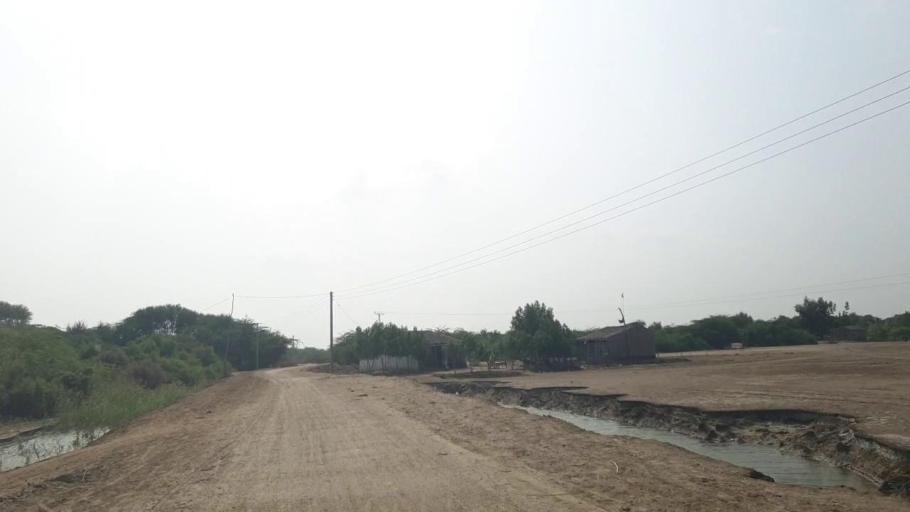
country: PK
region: Sindh
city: Badin
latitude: 24.5454
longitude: 68.6551
